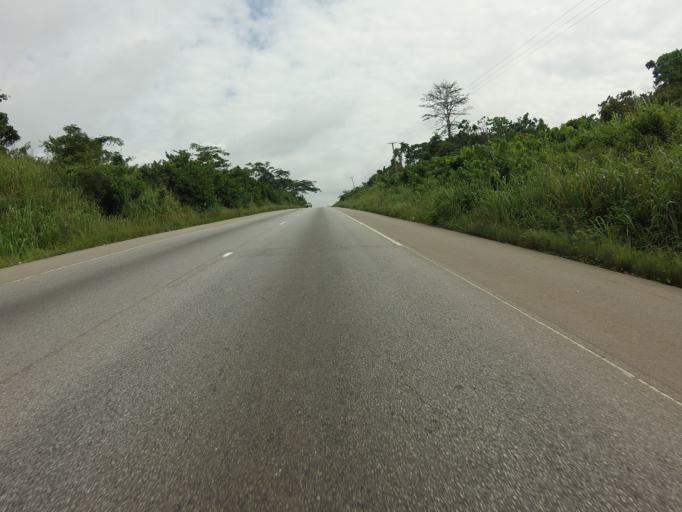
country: GH
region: Ashanti
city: Tafo
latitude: 6.9897
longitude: -1.6919
